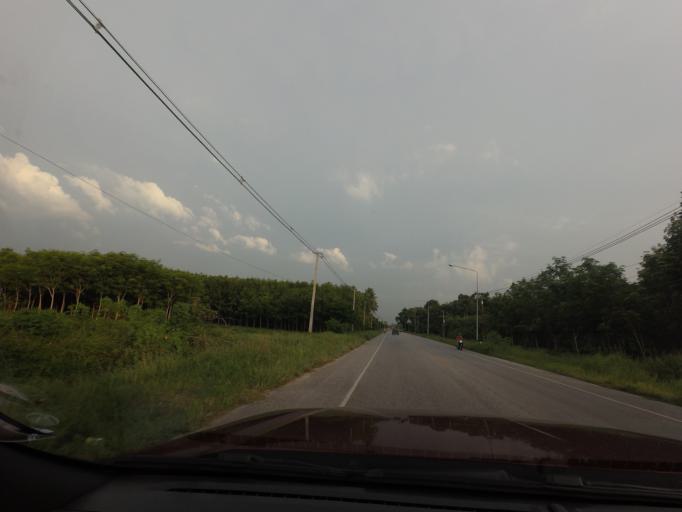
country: TH
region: Pattani
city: Mae Lan
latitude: 6.6291
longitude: 101.1874
